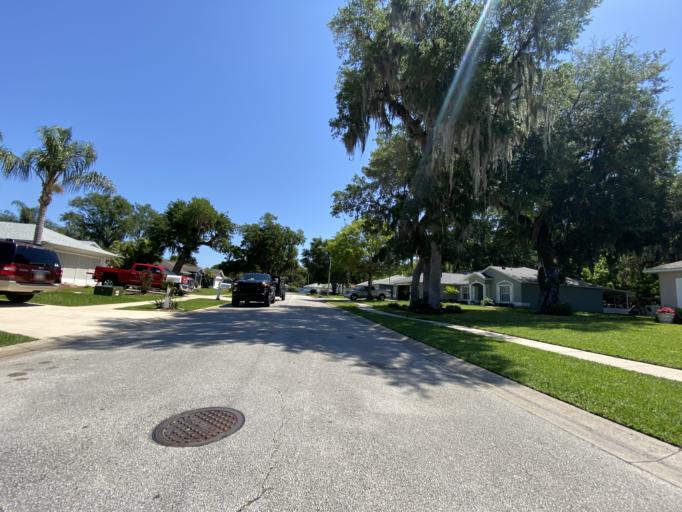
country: US
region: Florida
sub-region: Volusia County
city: Port Orange
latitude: 29.1492
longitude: -81.0046
